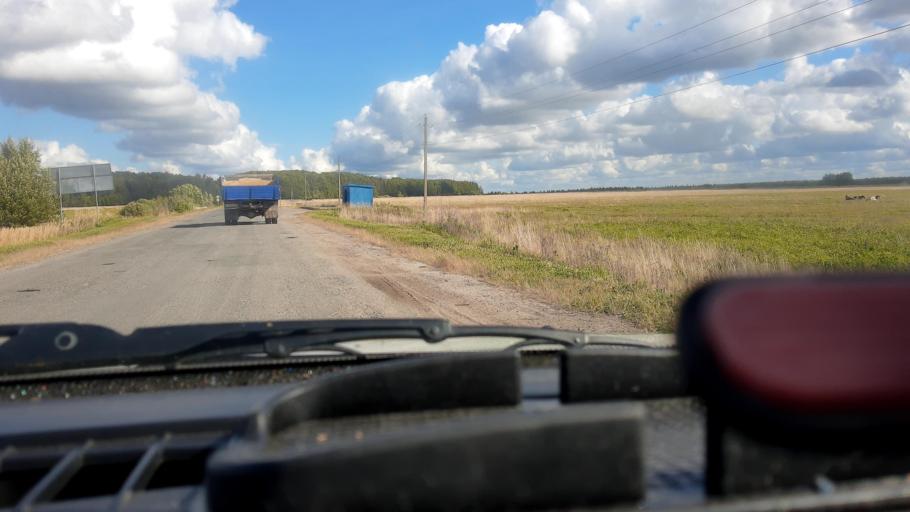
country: RU
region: Nizjnij Novgorod
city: Sharanga
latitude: 56.9378
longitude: 46.6528
